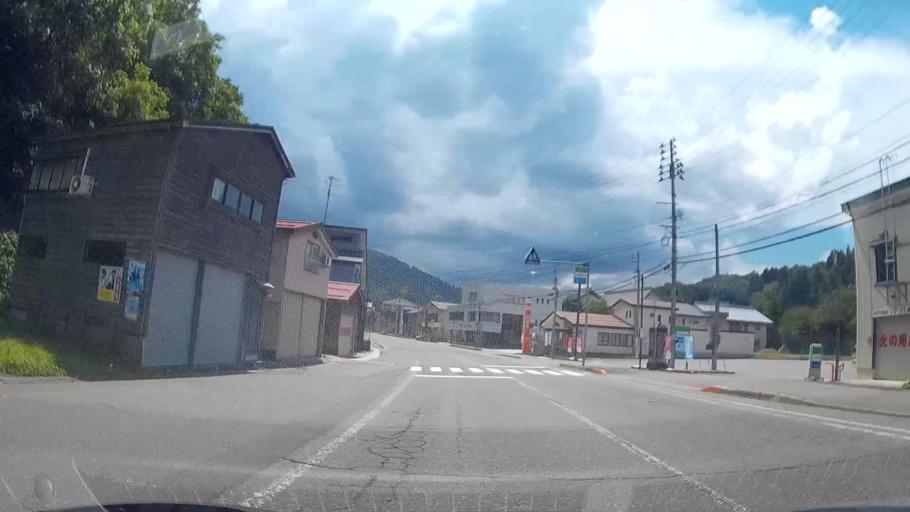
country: JP
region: Niigata
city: Tokamachi
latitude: 36.9925
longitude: 138.5902
